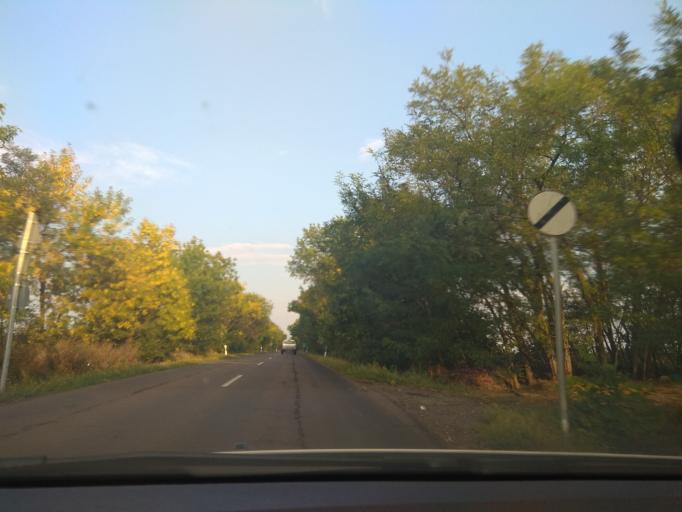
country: HU
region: Heves
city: Szihalom
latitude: 47.8198
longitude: 20.5004
